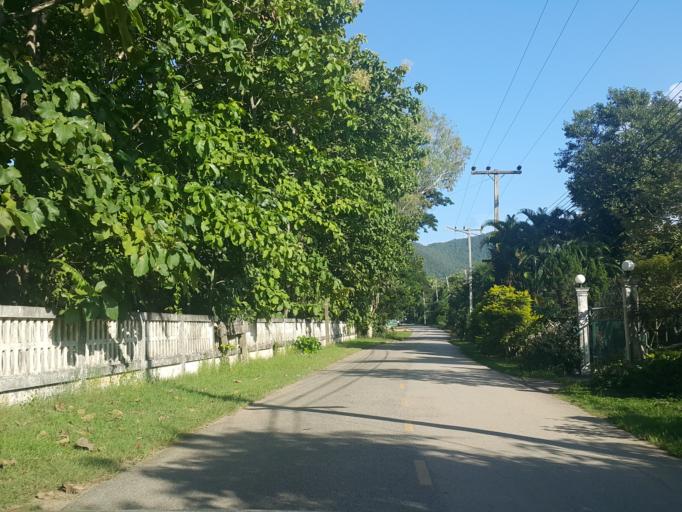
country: TH
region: Chiang Mai
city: Mae On
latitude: 18.7228
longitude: 99.2061
